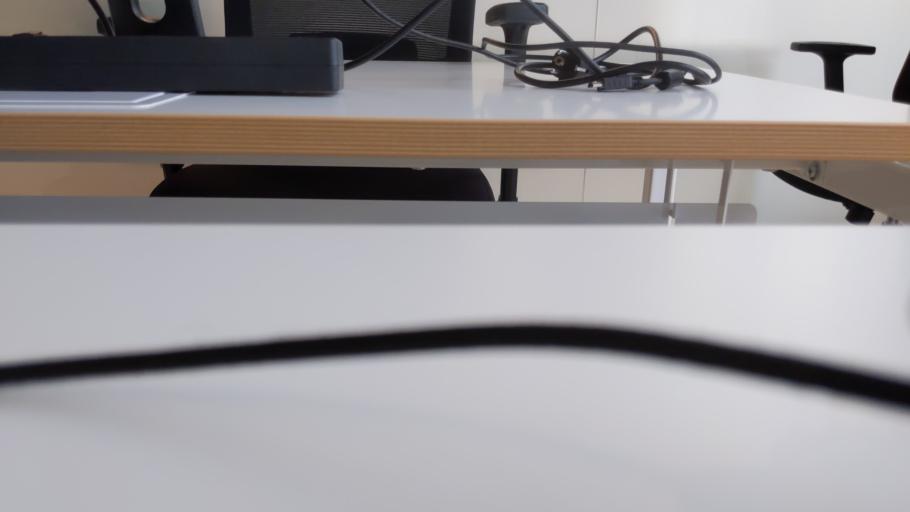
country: RU
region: Moskovskaya
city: Rogachevo
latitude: 56.4184
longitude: 37.0248
